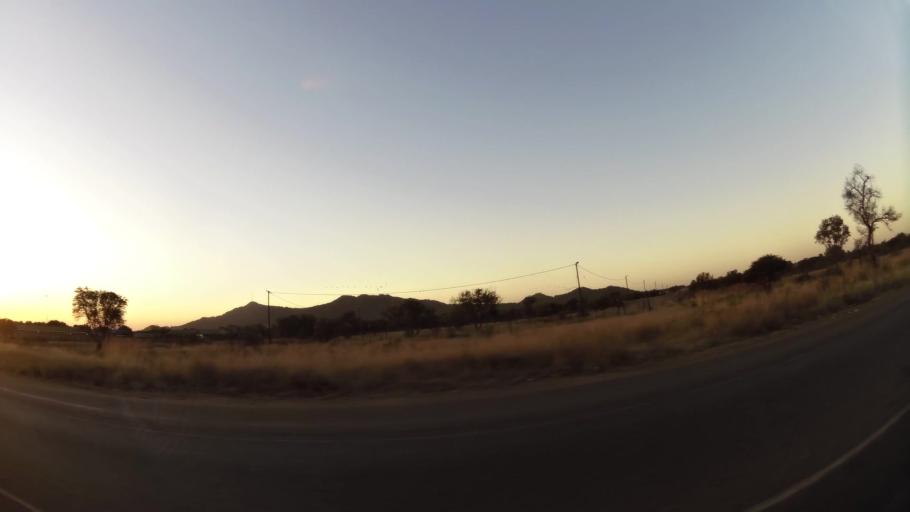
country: ZA
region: North-West
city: Ga-Rankuwa
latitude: -25.6220
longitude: 28.0262
